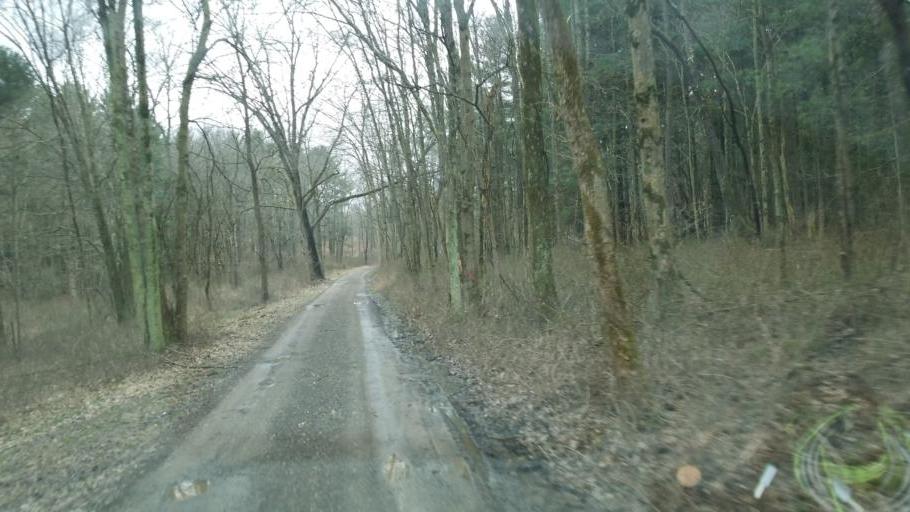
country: US
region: Ohio
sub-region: Ashland County
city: Loudonville
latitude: 40.5749
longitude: -82.3448
